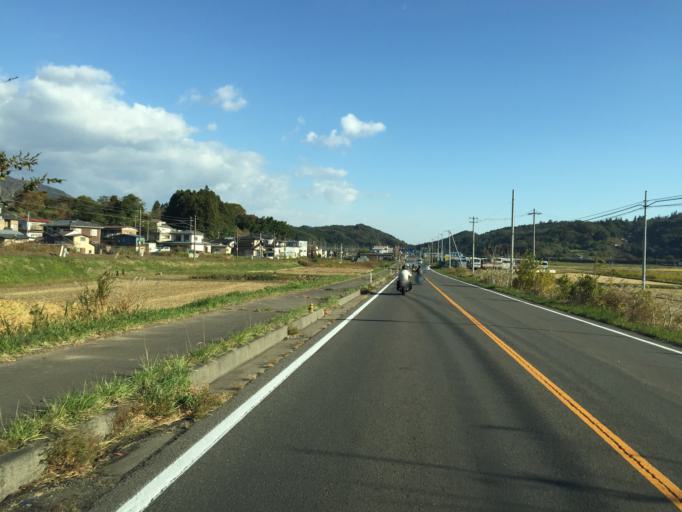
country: JP
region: Fukushima
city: Yanagawamachi-saiwaicho
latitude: 37.9274
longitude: 140.6032
